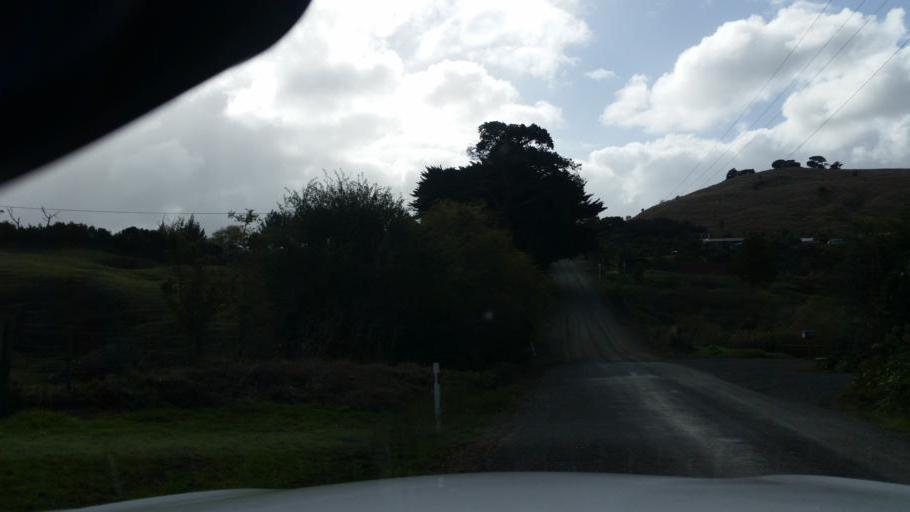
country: NZ
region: Northland
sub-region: Whangarei
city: Ruakaka
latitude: -36.1015
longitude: 174.3671
